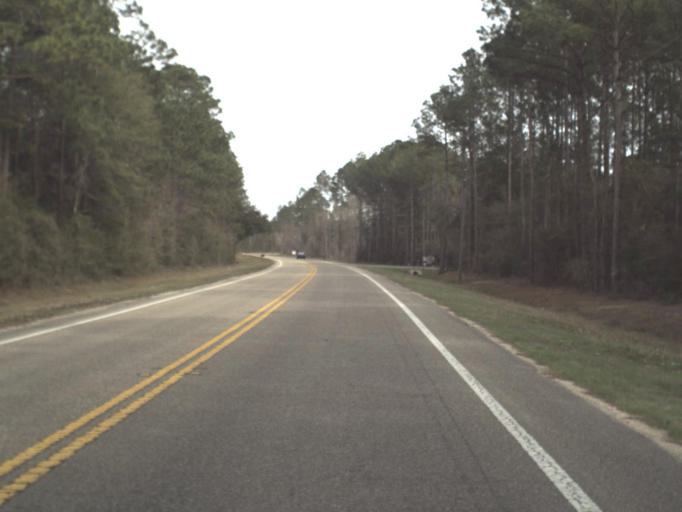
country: US
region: Florida
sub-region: Leon County
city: Woodville
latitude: 30.2261
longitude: -84.2134
